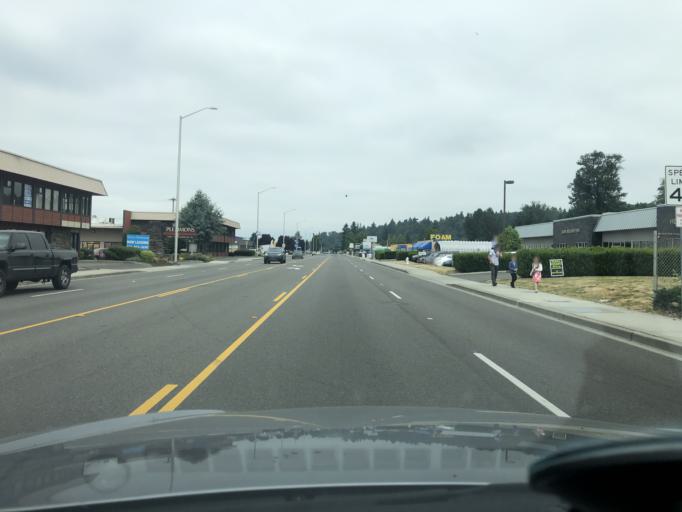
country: US
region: Washington
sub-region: King County
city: Kent
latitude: 47.3646
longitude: -122.2299
